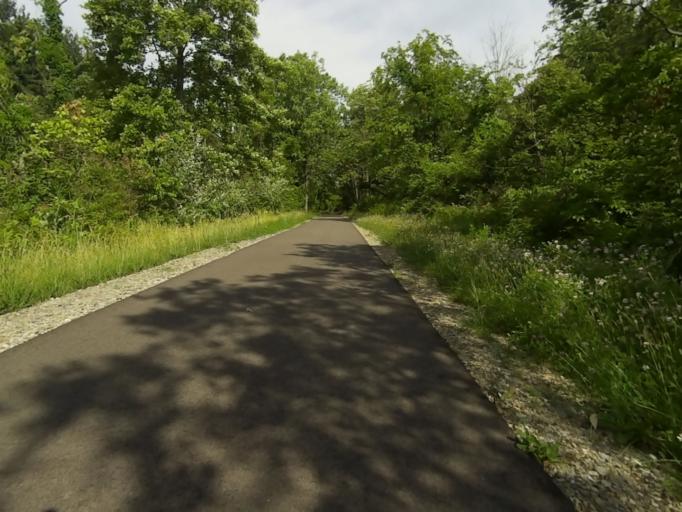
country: US
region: Ohio
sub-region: Summit County
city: Boston Heights
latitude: 41.2351
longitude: -81.4992
